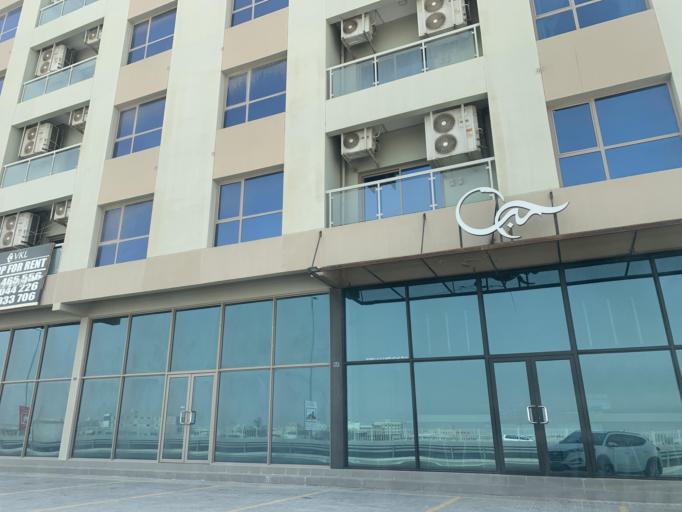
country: BH
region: Northern
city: Madinat `Isa
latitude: 26.1894
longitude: 50.5180
